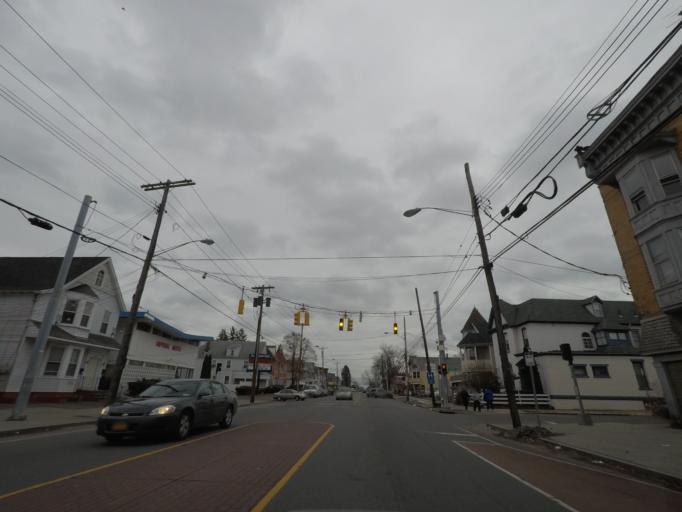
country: US
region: New York
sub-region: Schenectady County
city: Schenectady
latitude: 42.8051
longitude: -73.9321
